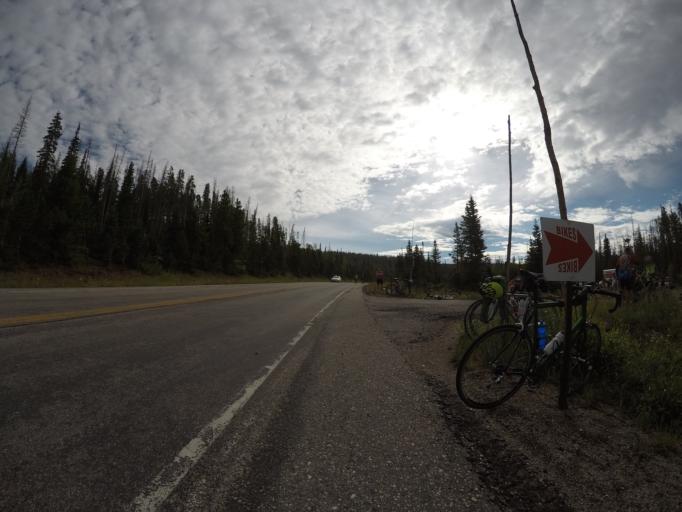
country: US
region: Wyoming
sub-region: Carbon County
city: Saratoga
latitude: 41.3266
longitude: -106.4972
